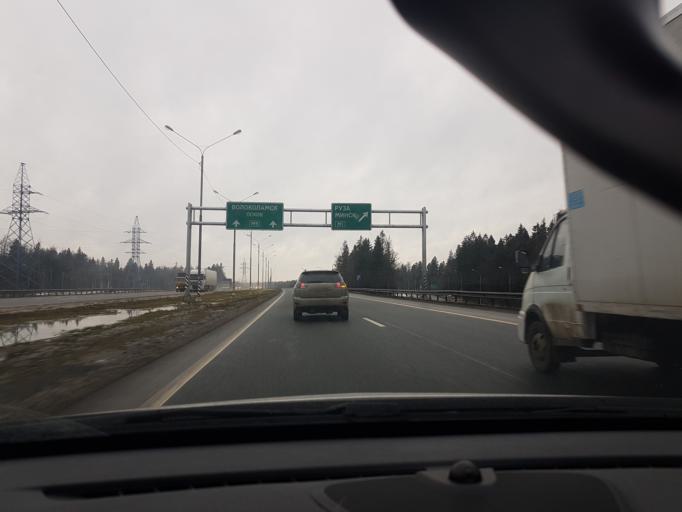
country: RU
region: Moskovskaya
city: Novopetrovskoye
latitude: 55.9806
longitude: 36.4492
